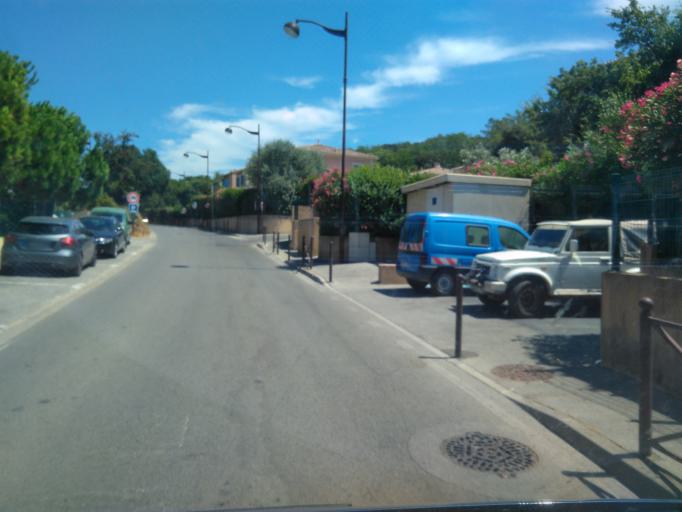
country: FR
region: Provence-Alpes-Cote d'Azur
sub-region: Departement du Var
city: La Croix-Valmer
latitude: 43.2095
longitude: 6.5708
